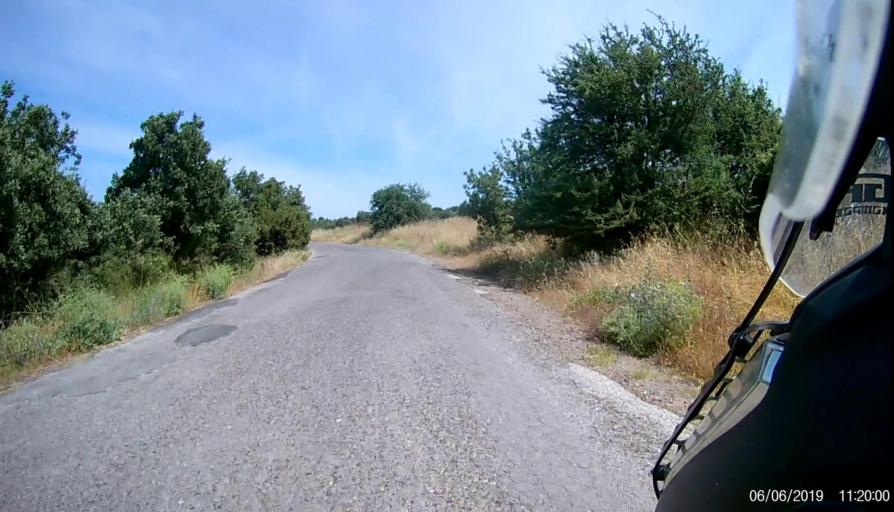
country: TR
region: Canakkale
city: Gulpinar
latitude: 39.6621
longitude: 26.1639
